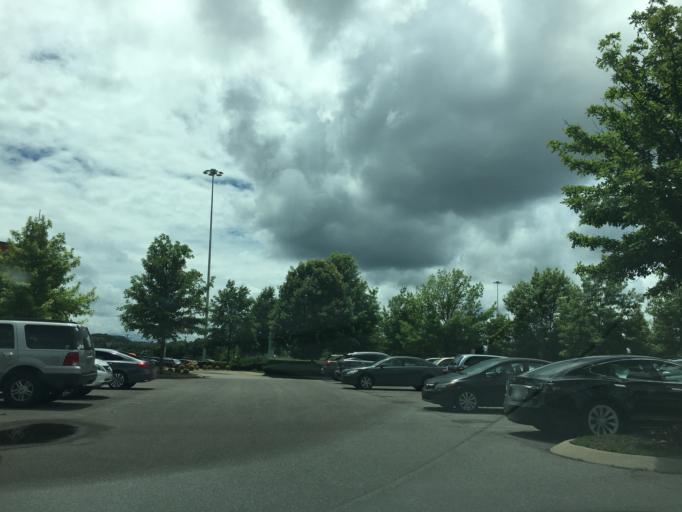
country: US
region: Tennessee
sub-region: Davidson County
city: Oak Hill
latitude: 36.1070
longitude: -86.7613
